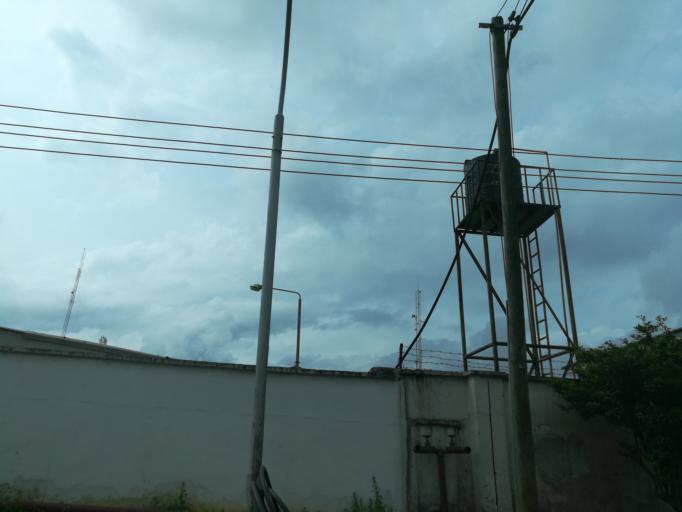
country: NG
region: Lagos
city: Ikeja
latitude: 6.5915
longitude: 3.3349
